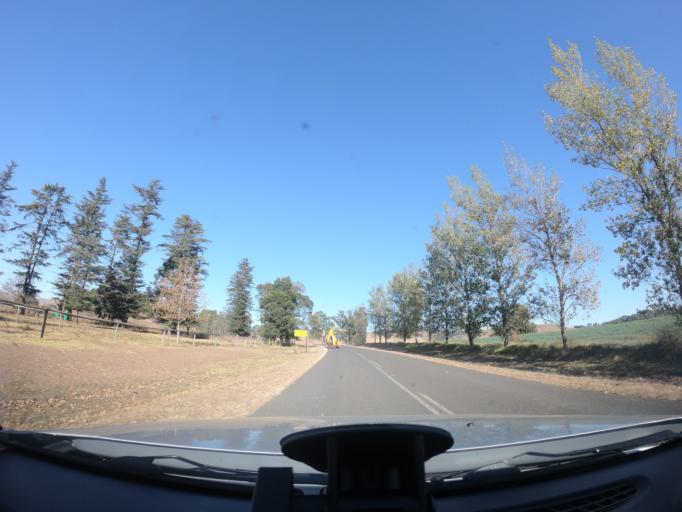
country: ZA
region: KwaZulu-Natal
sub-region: uMgungundlovu District Municipality
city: Mooirivier
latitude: -29.3168
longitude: 29.9222
